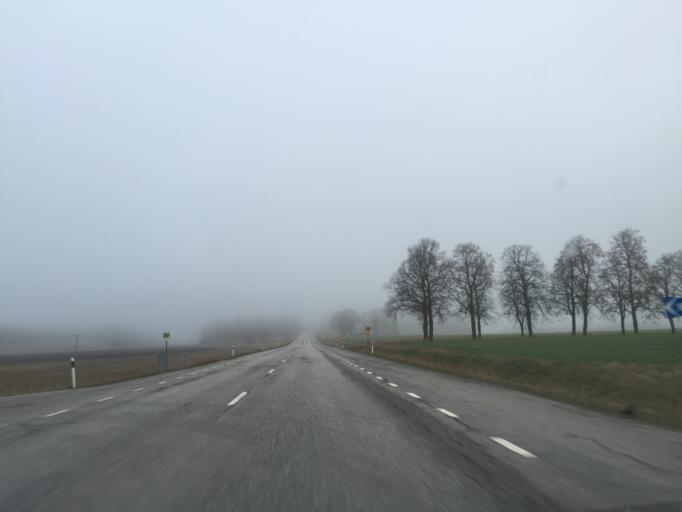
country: SE
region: Soedermanland
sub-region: Nykopings Kommun
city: Stigtomta
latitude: 58.8336
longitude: 16.7500
